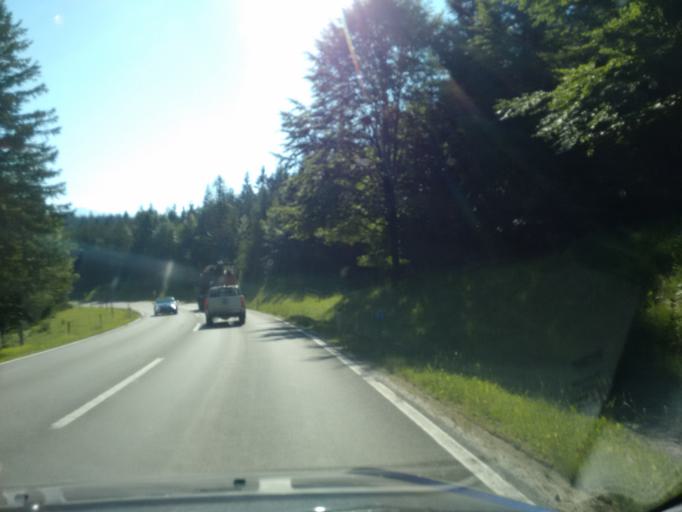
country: AT
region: Styria
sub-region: Politischer Bezirk Liezen
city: Altaussee
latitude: 47.6217
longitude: 13.6993
